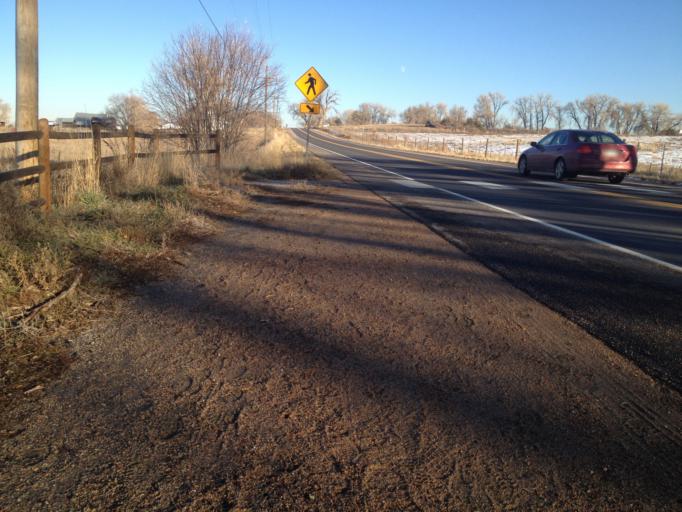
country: US
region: Colorado
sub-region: Boulder County
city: Gunbarrel
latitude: 40.0401
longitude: -105.1459
